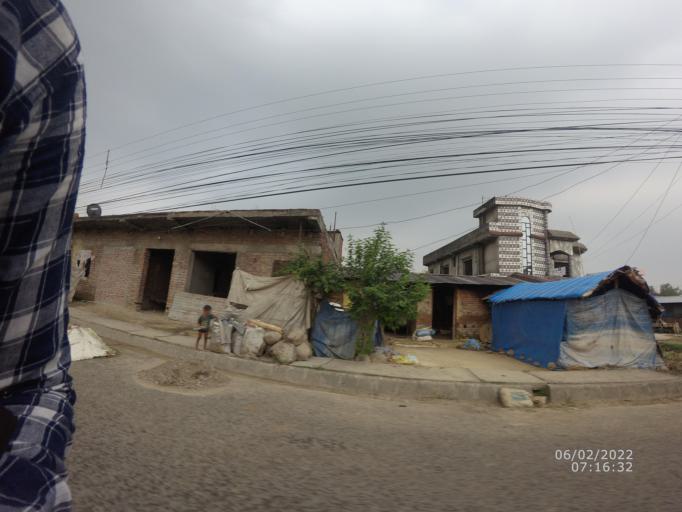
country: NP
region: Western Region
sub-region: Lumbini Zone
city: Bhairahawa
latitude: 27.4850
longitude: 83.4394
